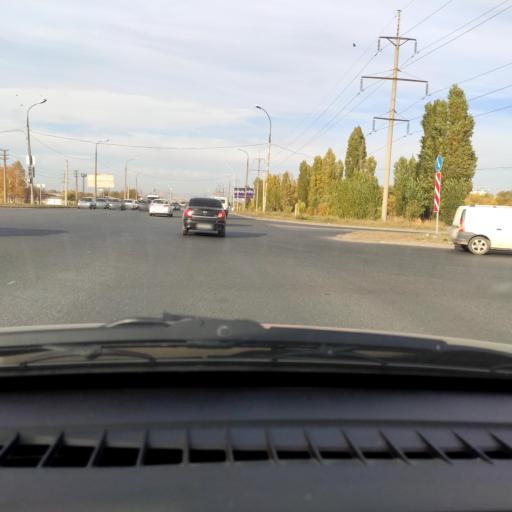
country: RU
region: Samara
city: Tol'yatti
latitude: 53.5609
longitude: 49.2896
